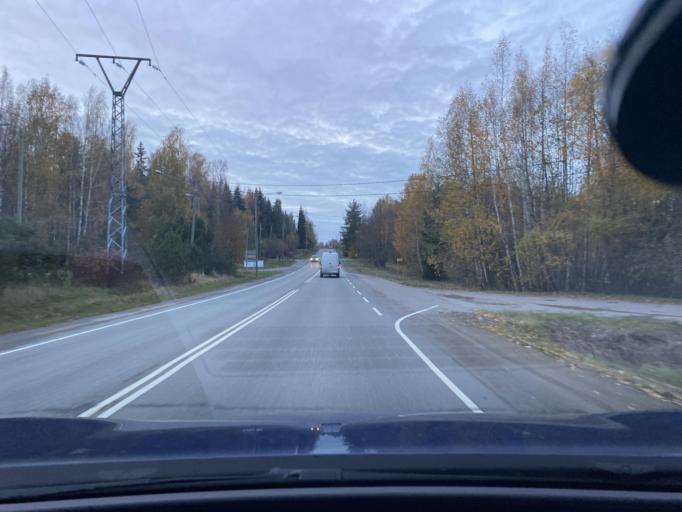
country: FI
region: Uusimaa
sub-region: Helsinki
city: Lohja
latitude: 60.3632
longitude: 24.1669
